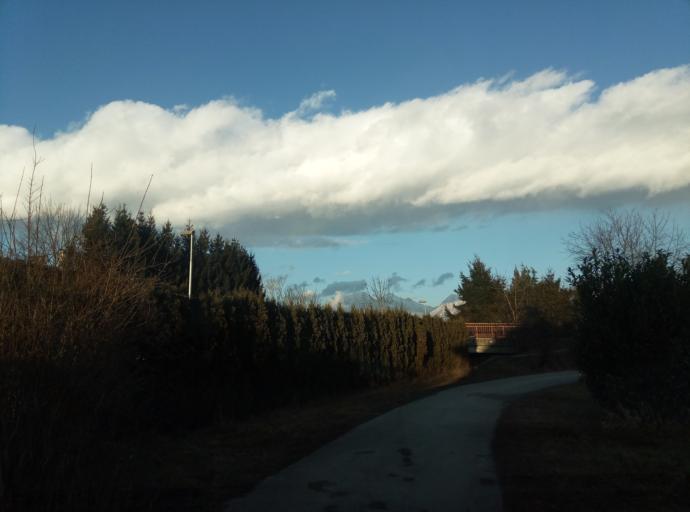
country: SI
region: Kranj
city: Kranj
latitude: 46.2291
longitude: 14.3650
